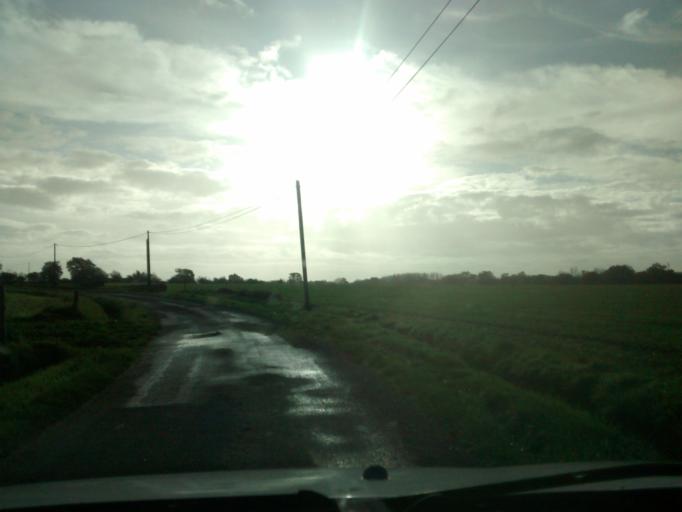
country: FR
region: Brittany
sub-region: Departement d'Ille-et-Vilaine
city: Noyal-sur-Vilaine
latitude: 48.1268
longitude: -1.5168
